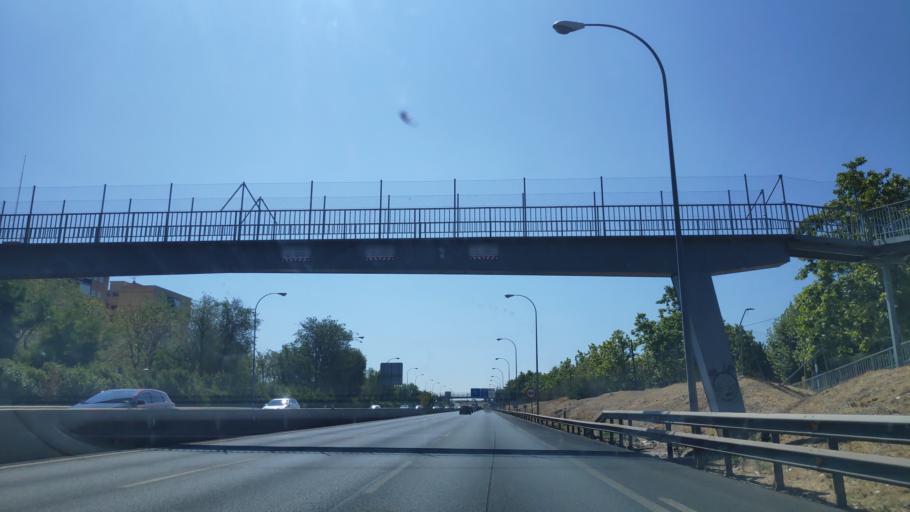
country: ES
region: Madrid
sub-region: Provincia de Madrid
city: Getafe
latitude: 40.3023
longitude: -3.7389
